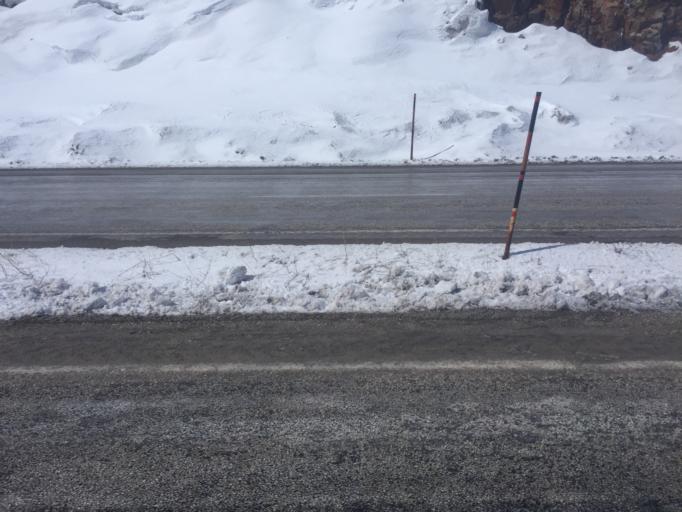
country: TR
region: Kahramanmaras
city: Goksun
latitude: 38.1911
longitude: 36.4569
